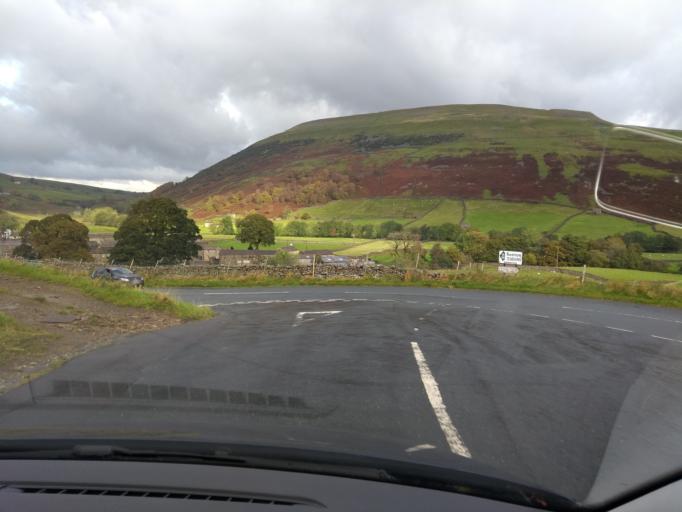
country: GB
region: England
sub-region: County Durham
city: Bowes
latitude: 54.3772
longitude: -2.1664
